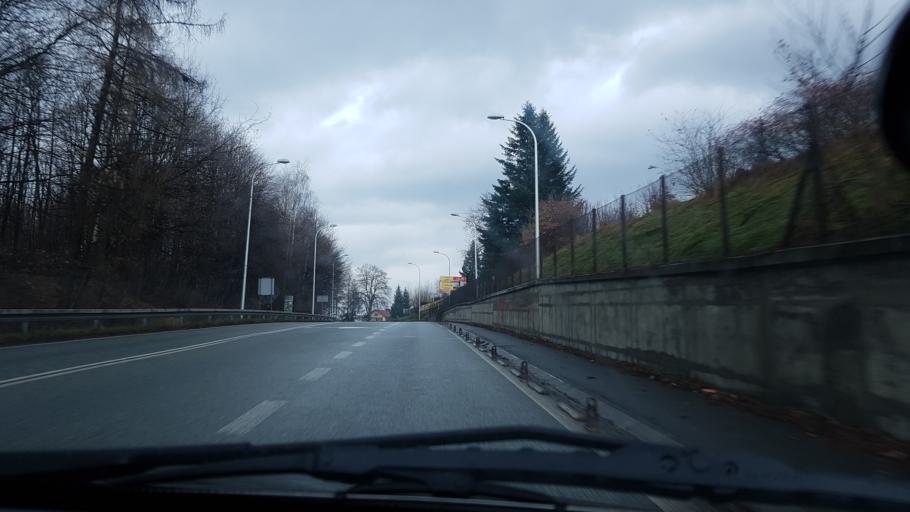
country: PL
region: Silesian Voivodeship
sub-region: Powiat zywiecki
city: Zywiec
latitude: 49.7047
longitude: 19.2058
